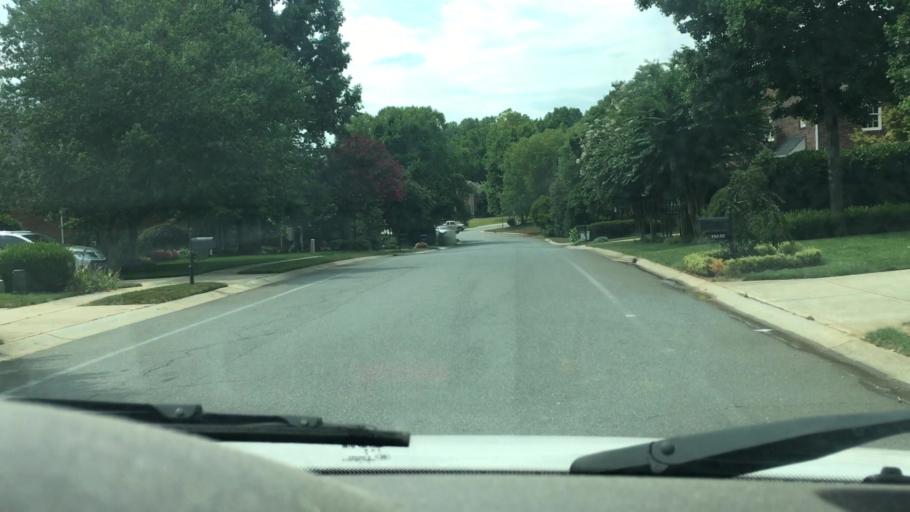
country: US
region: North Carolina
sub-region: Gaston County
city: Davidson
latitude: 35.4707
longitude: -80.7858
